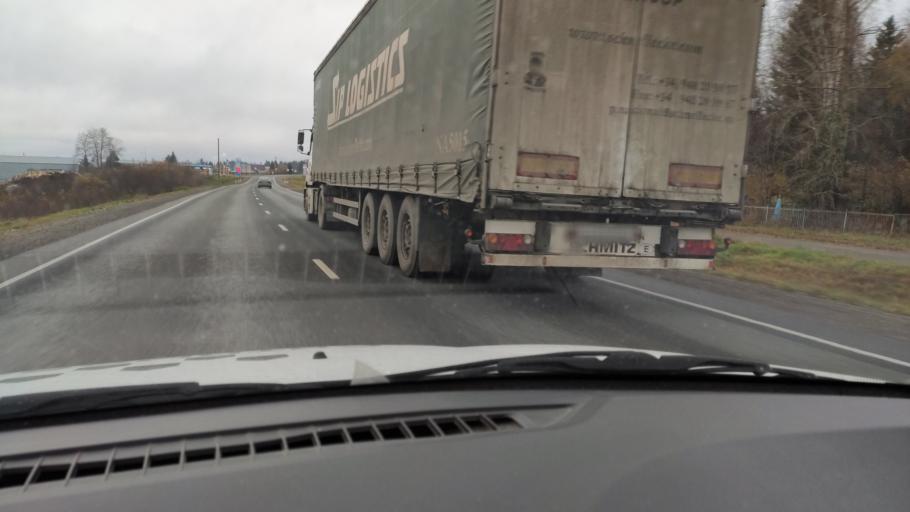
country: RU
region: Kirov
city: Omutninsk
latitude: 58.6914
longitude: 52.1939
